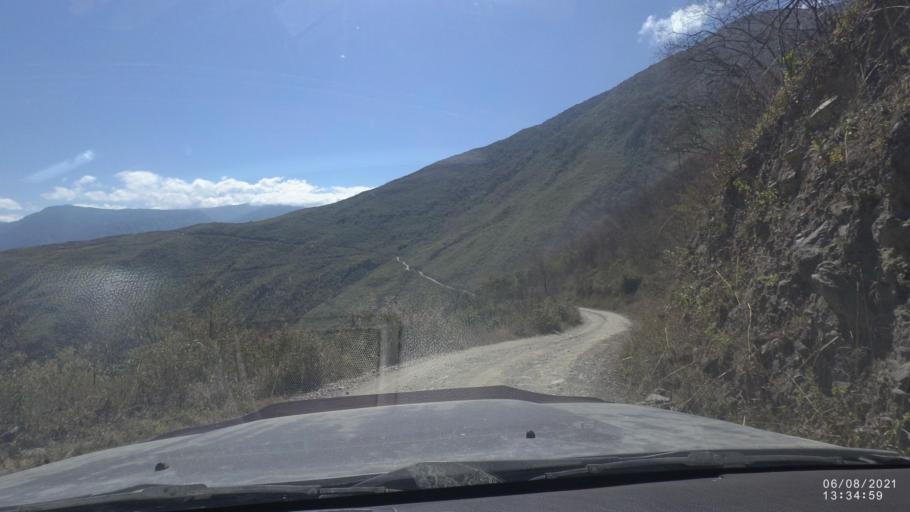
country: BO
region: La Paz
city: Quime
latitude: -16.6937
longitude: -66.7224
